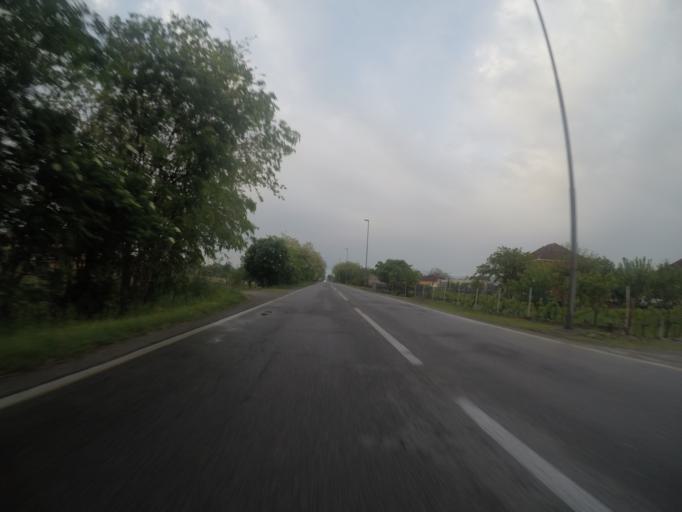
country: ME
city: Mojanovici
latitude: 42.3400
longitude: 19.2215
